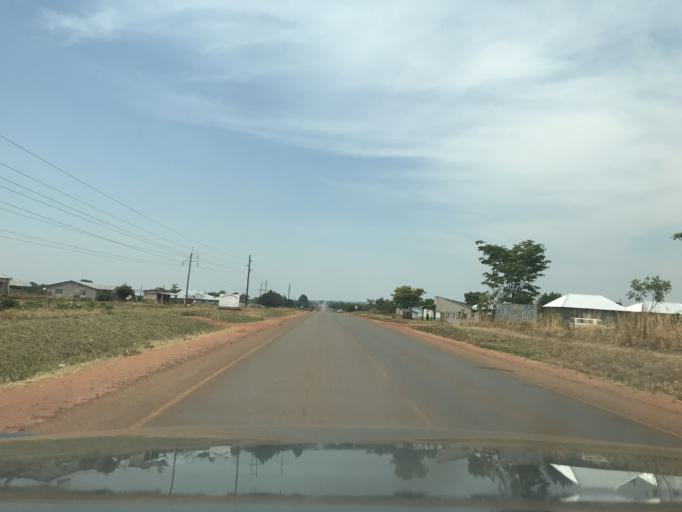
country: ZM
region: Northern
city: Kasama
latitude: -10.2088
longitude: 31.1693
